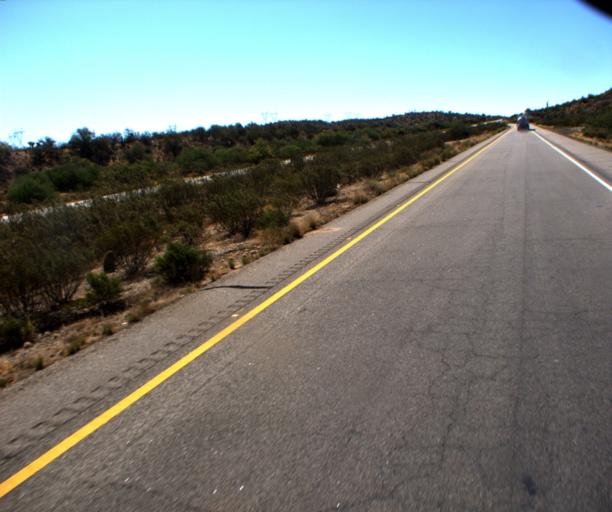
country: US
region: Arizona
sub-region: Yavapai County
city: Bagdad
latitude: 34.3647
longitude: -113.1762
